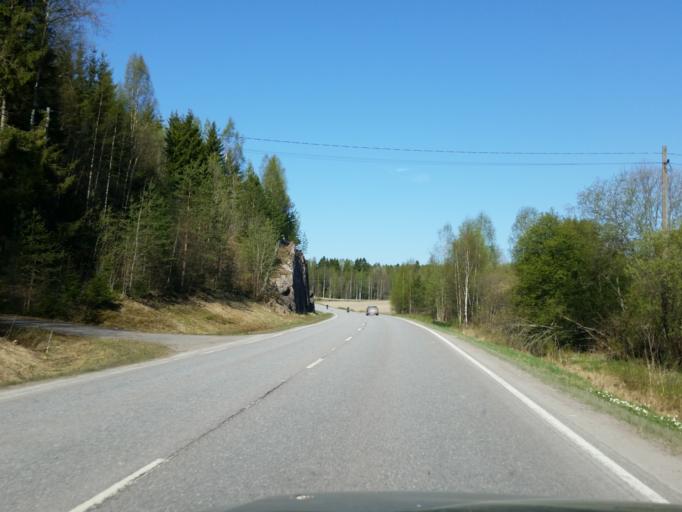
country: FI
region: Uusimaa
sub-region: Helsinki
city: Siuntio
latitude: 60.1891
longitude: 24.2846
